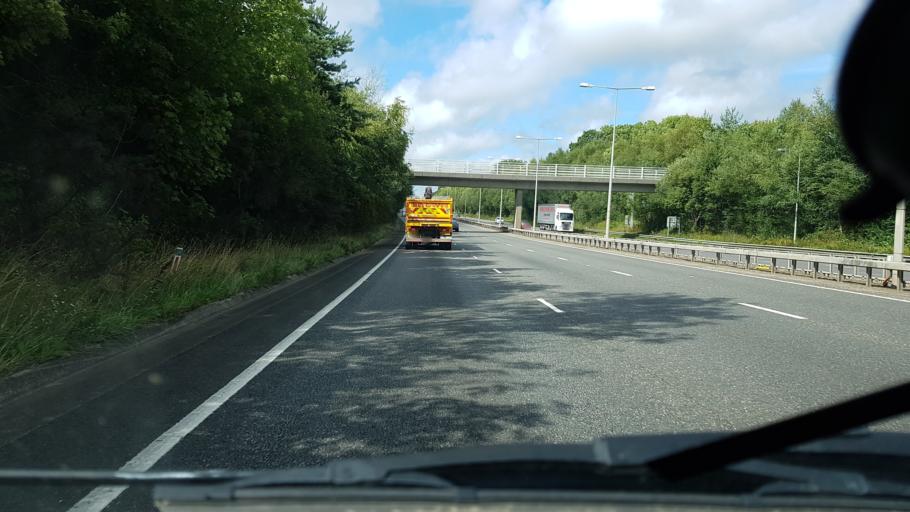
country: GB
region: England
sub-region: West Sussex
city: Broadfield
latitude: 51.0589
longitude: -0.2028
